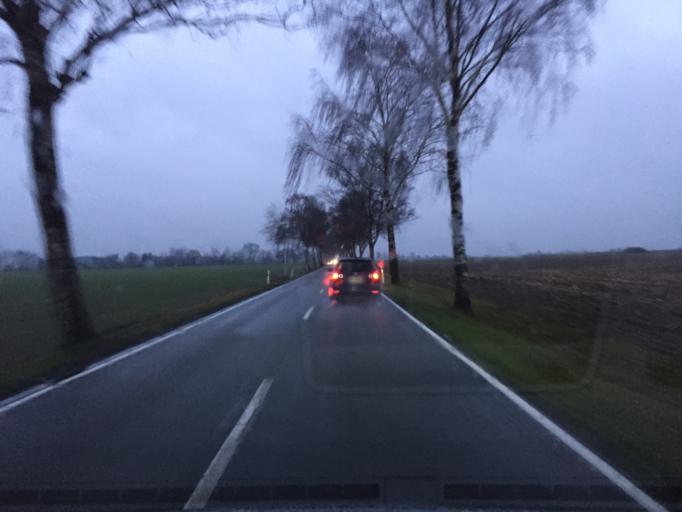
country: DE
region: Lower Saxony
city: Sustedt
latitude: 52.8669
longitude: 8.8598
